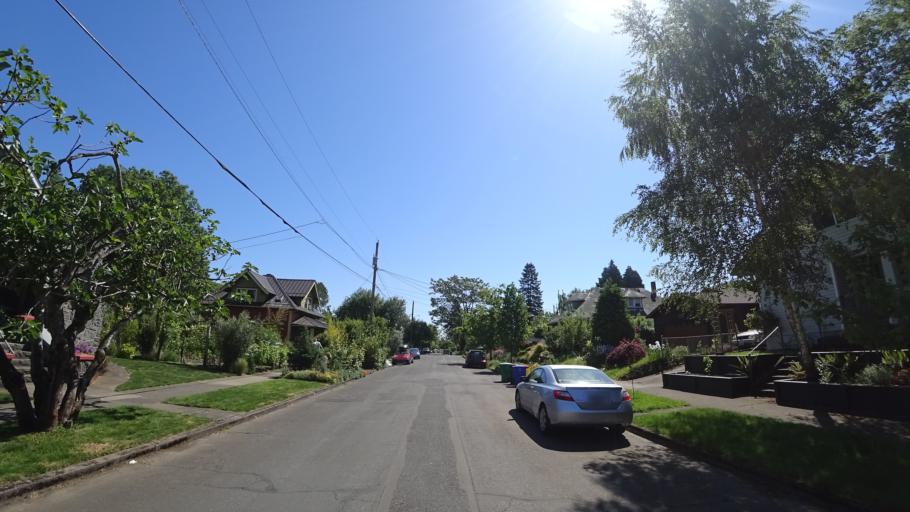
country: US
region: Oregon
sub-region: Clackamas County
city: Milwaukie
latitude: 45.4857
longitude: -122.6174
